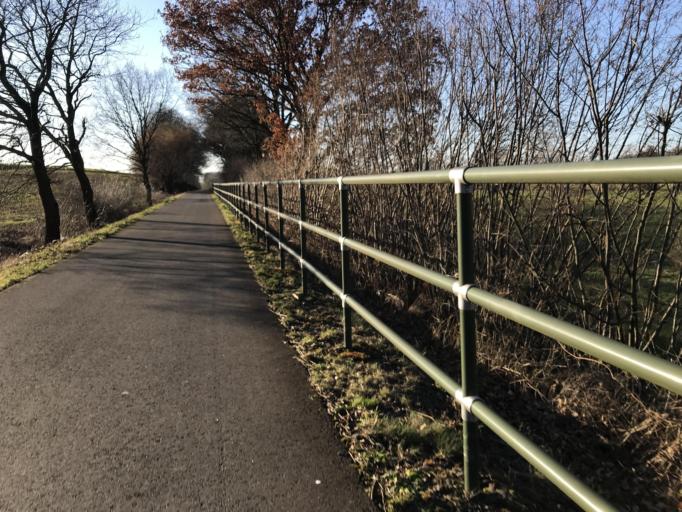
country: DE
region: Hesse
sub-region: Regierungsbezirk Kassel
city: Schrecksbach
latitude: 50.8725
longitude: 9.2904
